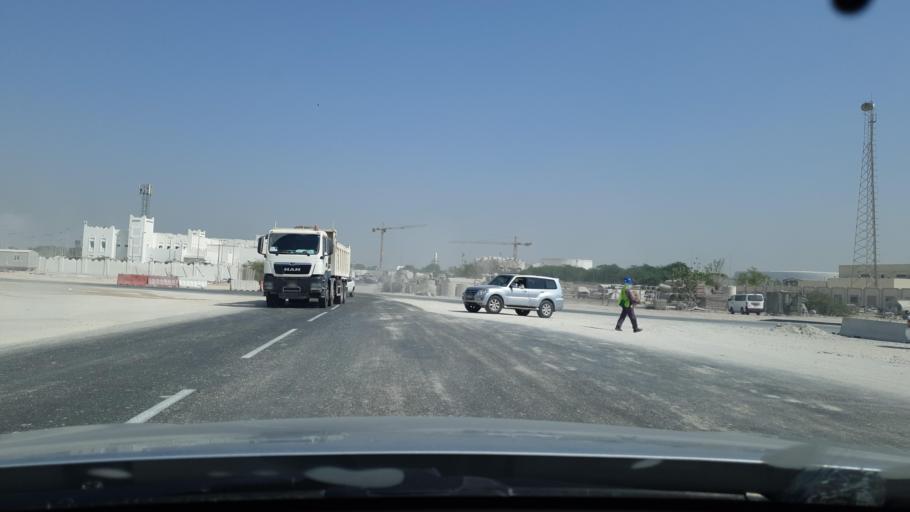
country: QA
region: Baladiyat ad Dawhah
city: Doha
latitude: 25.2289
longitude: 51.5215
